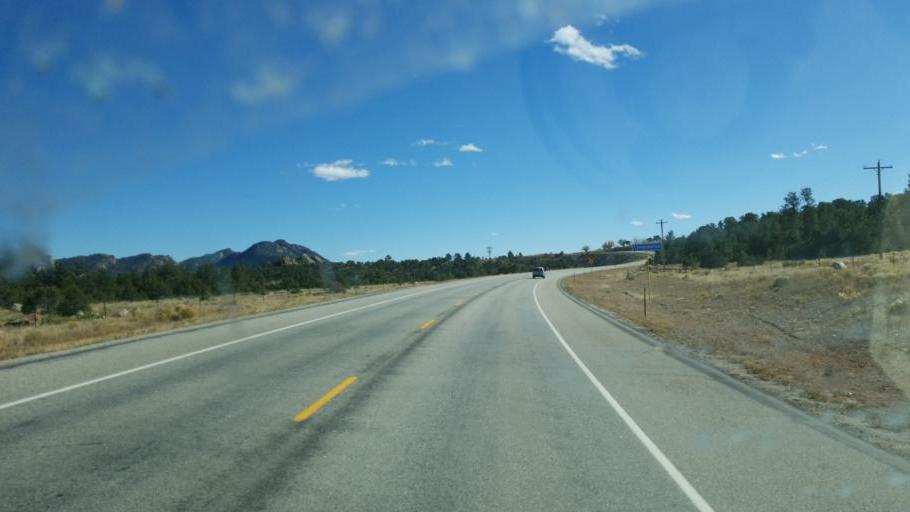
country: US
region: Colorado
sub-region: Chaffee County
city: Buena Vista
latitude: 38.8885
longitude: -106.1677
